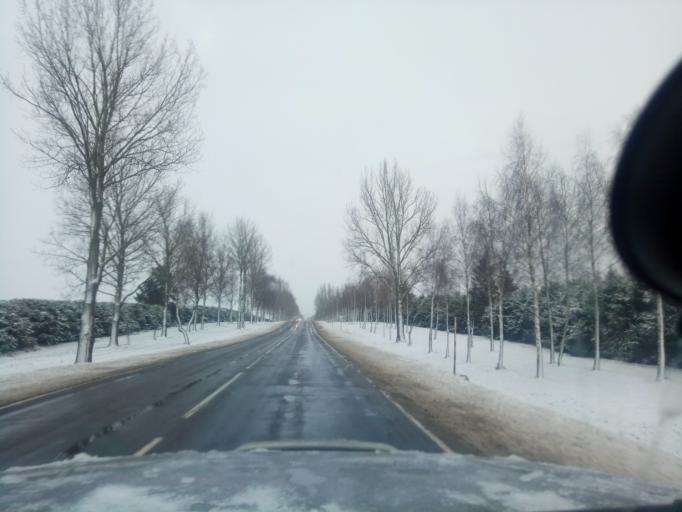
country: BY
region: Minsk
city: Haradzyeya
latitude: 53.3513
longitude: 26.5170
